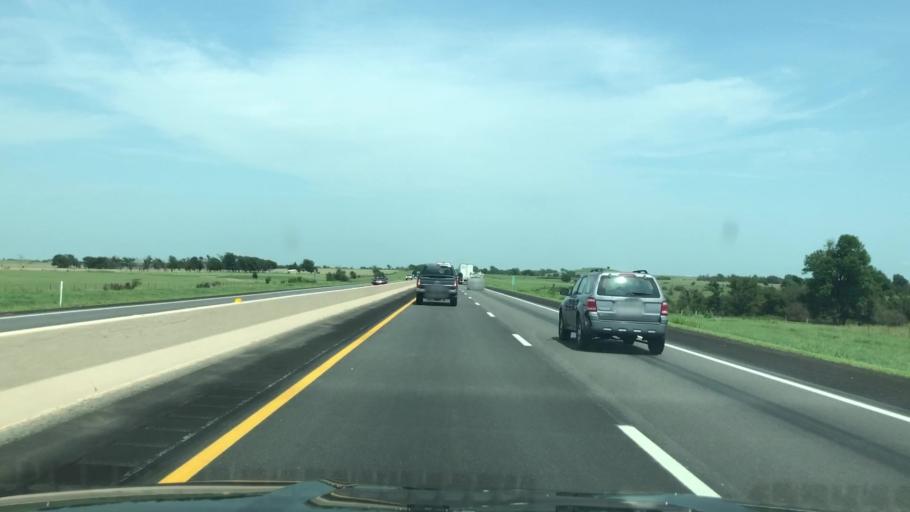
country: US
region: Oklahoma
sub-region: Ottawa County
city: Afton
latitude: 36.6776
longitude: -95.0508
